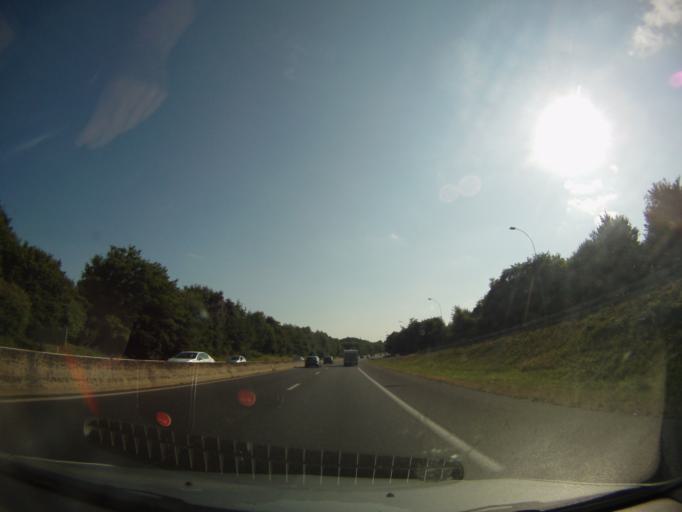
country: FR
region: Pays de la Loire
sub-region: Departement de la Loire-Atlantique
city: Carquefou
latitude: 47.2792
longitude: -1.5149
